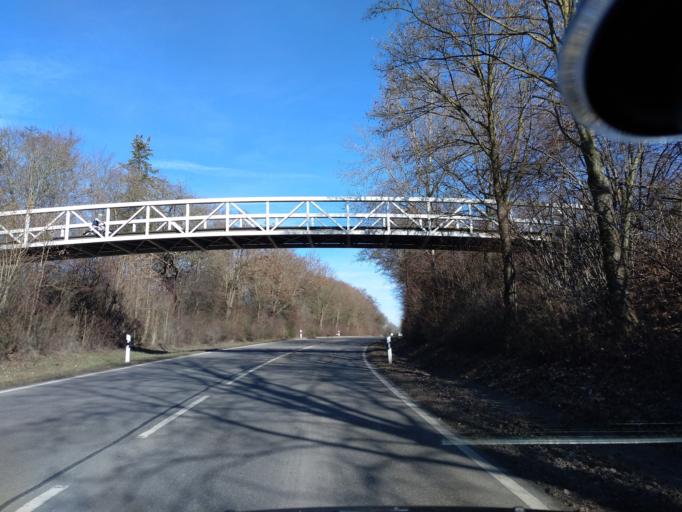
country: DE
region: Baden-Wuerttemberg
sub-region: Regierungsbezirk Stuttgart
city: Schwaebisch Hall
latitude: 49.0984
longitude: 9.7218
